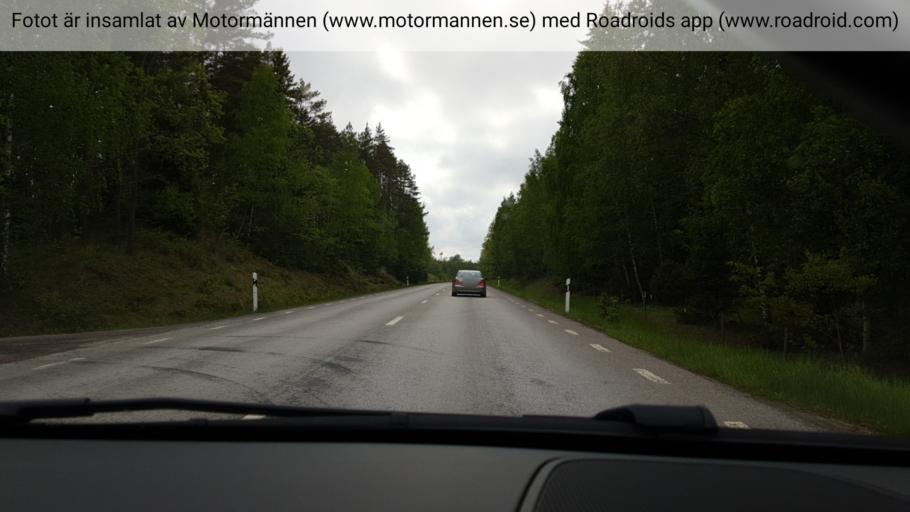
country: SE
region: Uppsala
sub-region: Osthammars Kommun
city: Osterbybruk
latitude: 60.1616
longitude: 18.0025
